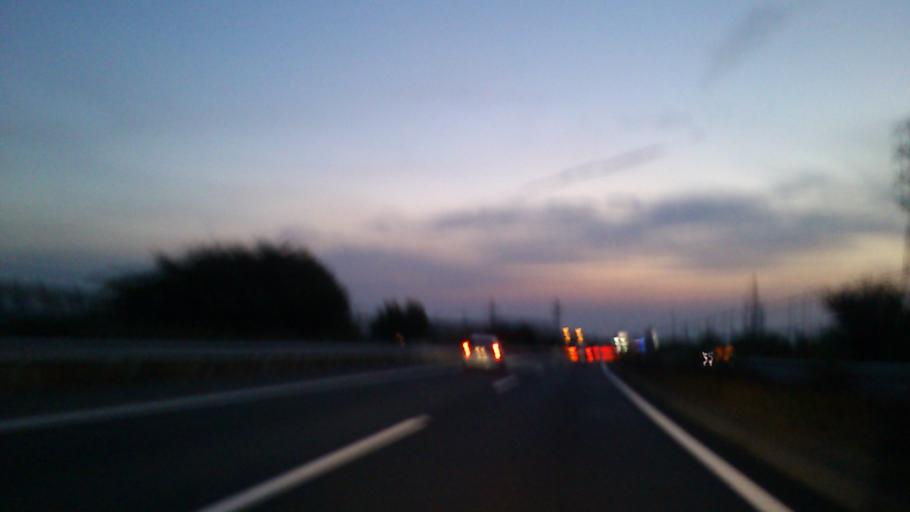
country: JP
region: Aichi
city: Komaki
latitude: 35.2914
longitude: 136.9537
